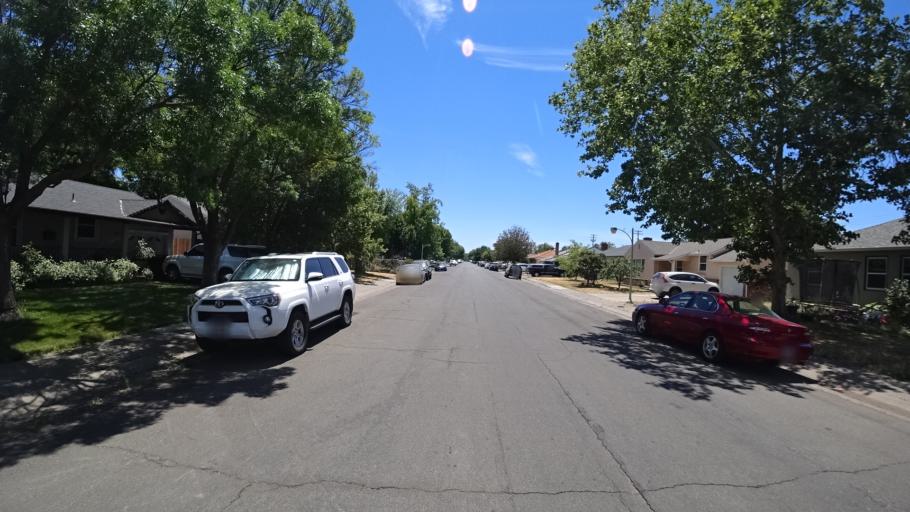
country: US
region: California
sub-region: Sacramento County
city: Parkway
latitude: 38.5232
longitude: -121.4399
